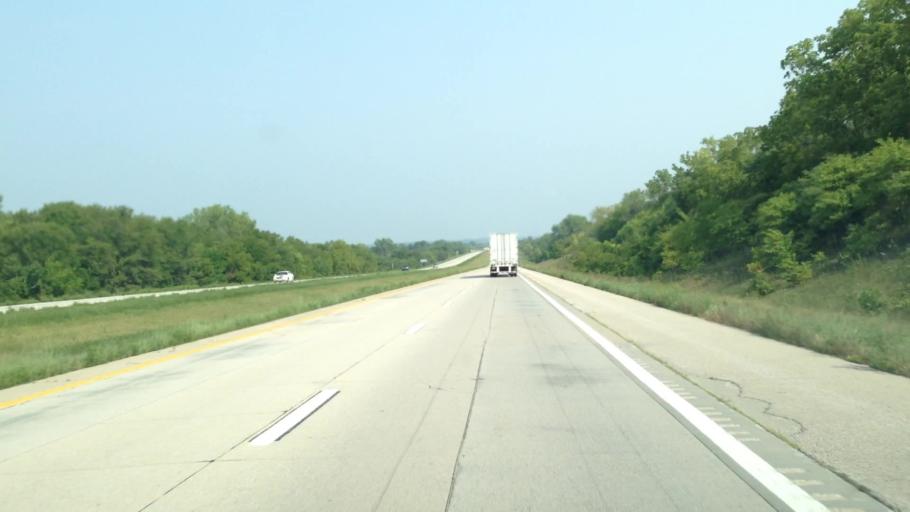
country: US
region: Missouri
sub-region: Daviess County
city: Gallatin
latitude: 39.9808
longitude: -94.0944
